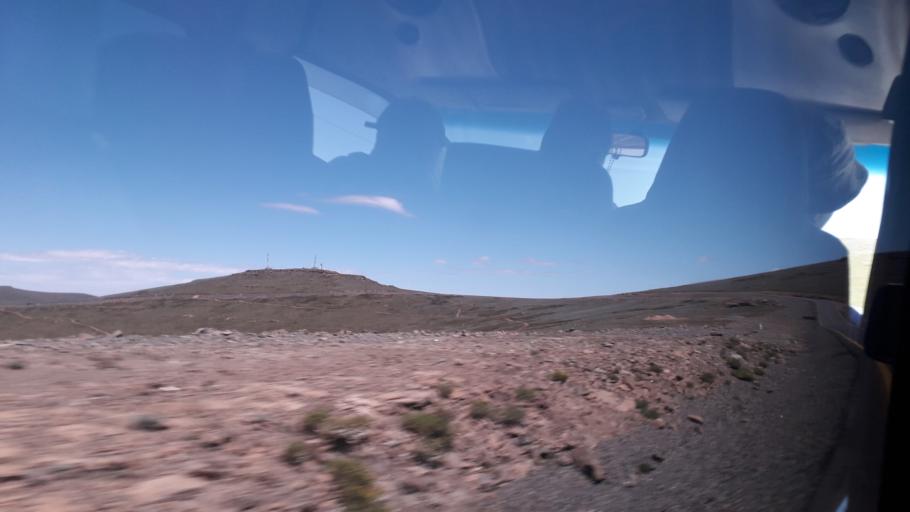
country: ZA
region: Orange Free State
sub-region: Thabo Mofutsanyana District Municipality
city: Phuthaditjhaba
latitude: -28.8127
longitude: 28.7349
